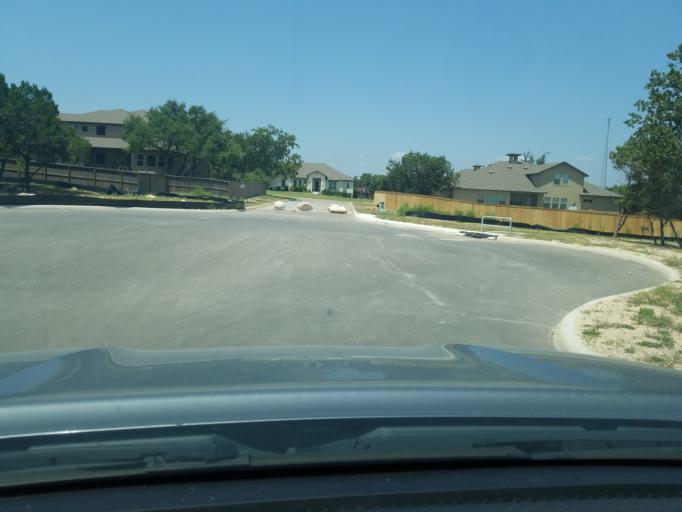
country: US
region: Texas
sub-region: Bexar County
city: Timberwood Park
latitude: 29.7129
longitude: -98.5071
